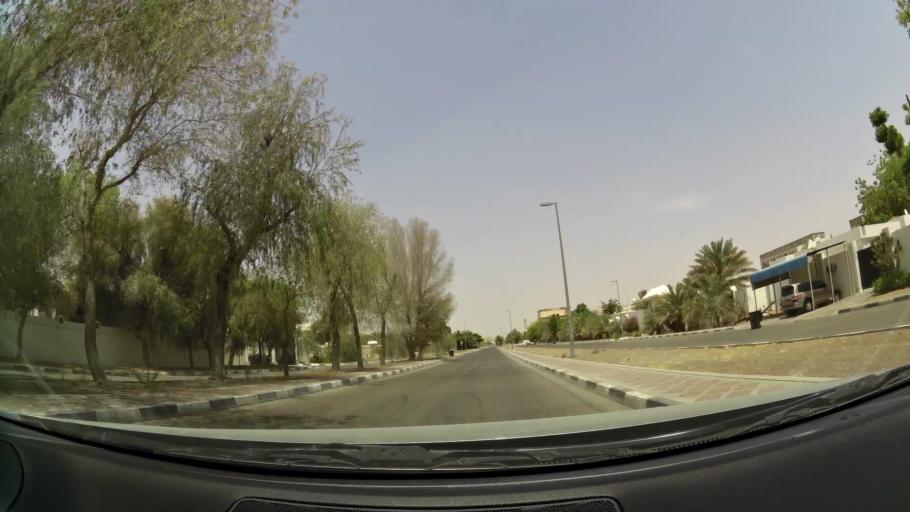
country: AE
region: Abu Dhabi
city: Al Ain
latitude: 24.1997
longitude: 55.7389
